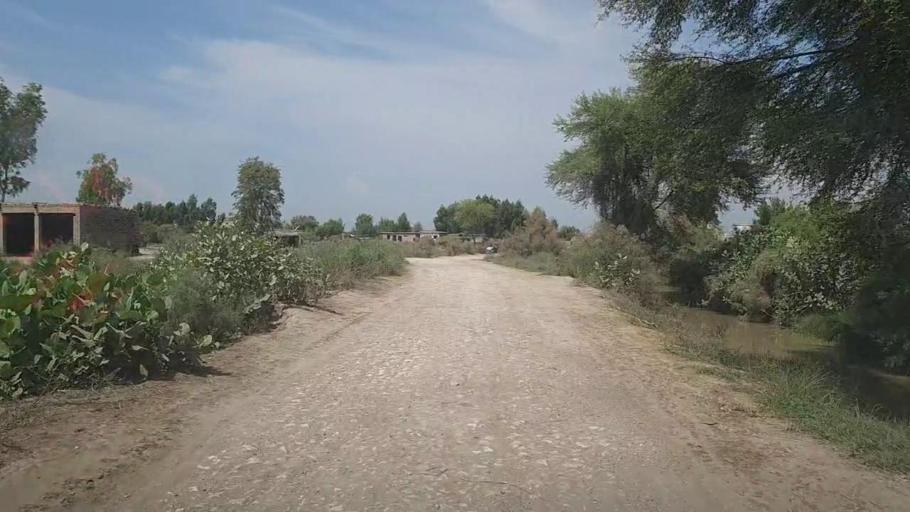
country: PK
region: Sindh
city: Kandhkot
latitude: 28.2779
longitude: 69.2347
